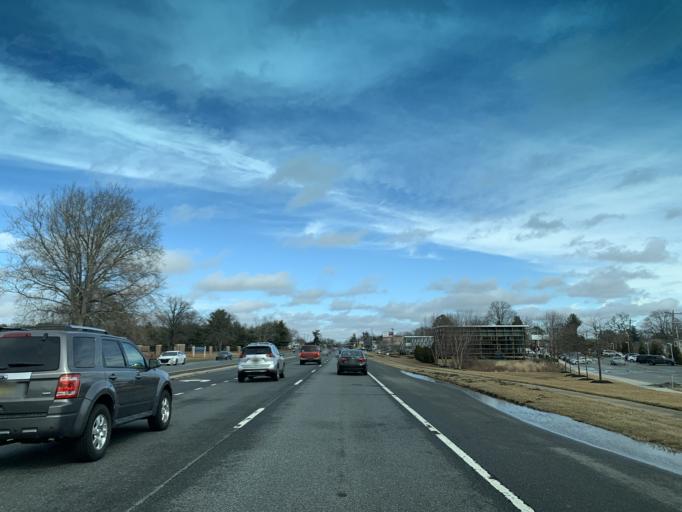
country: US
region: Delaware
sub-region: New Castle County
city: Pike Creek
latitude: 39.7100
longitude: -75.6805
